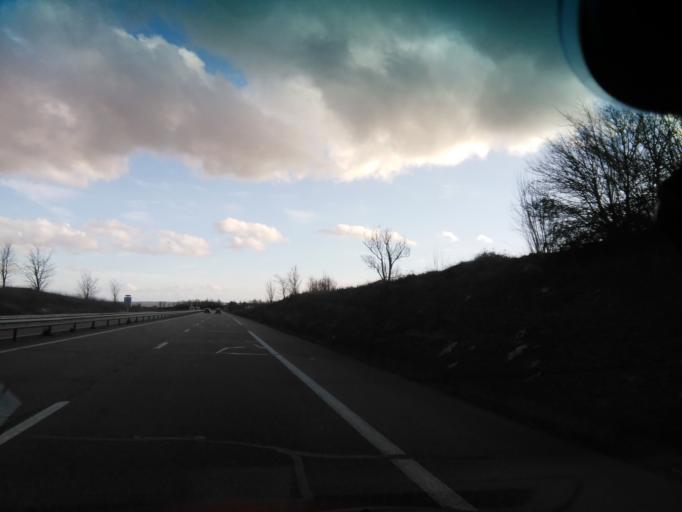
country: FR
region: Lower Normandy
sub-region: Departement du Calvados
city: Falaise
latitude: 48.9289
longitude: -0.2074
